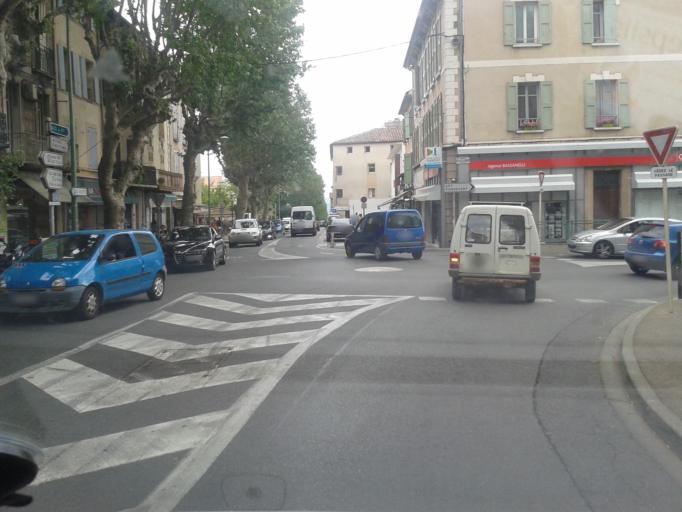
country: FR
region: Provence-Alpes-Cote d'Azur
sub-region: Departement des Alpes-de-Haute-Provence
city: Manosque
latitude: 43.8308
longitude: 5.7846
